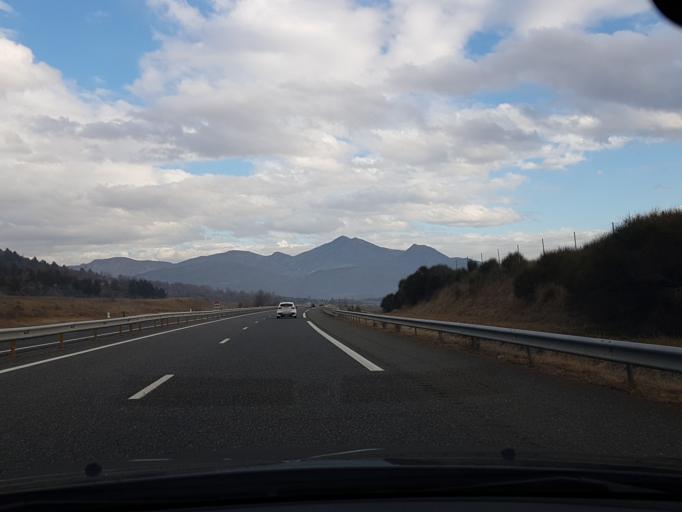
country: FR
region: Provence-Alpes-Cote d'Azur
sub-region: Departement des Hautes-Alpes
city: Tallard
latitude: 44.3945
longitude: 5.9437
